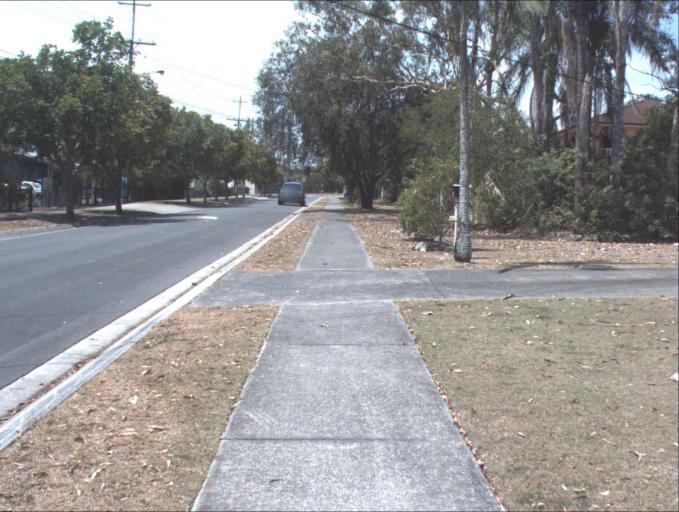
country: AU
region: Queensland
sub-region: Logan
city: Slacks Creek
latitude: -27.6644
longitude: 153.1791
